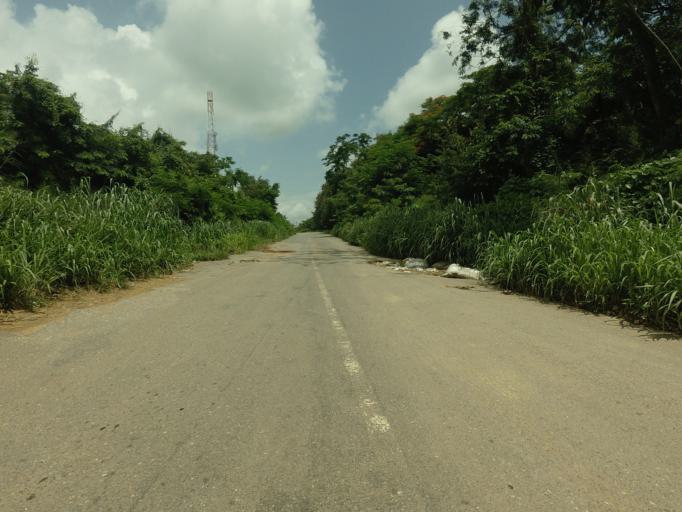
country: GH
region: Volta
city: Ho
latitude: 6.7175
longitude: 0.3390
